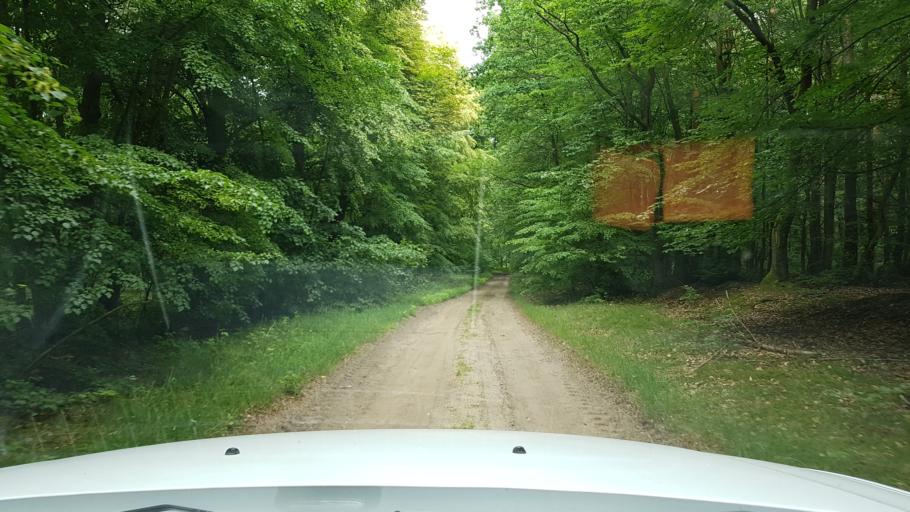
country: PL
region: West Pomeranian Voivodeship
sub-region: Powiat mysliborski
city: Boleszkowice
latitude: 52.6669
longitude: 14.5825
